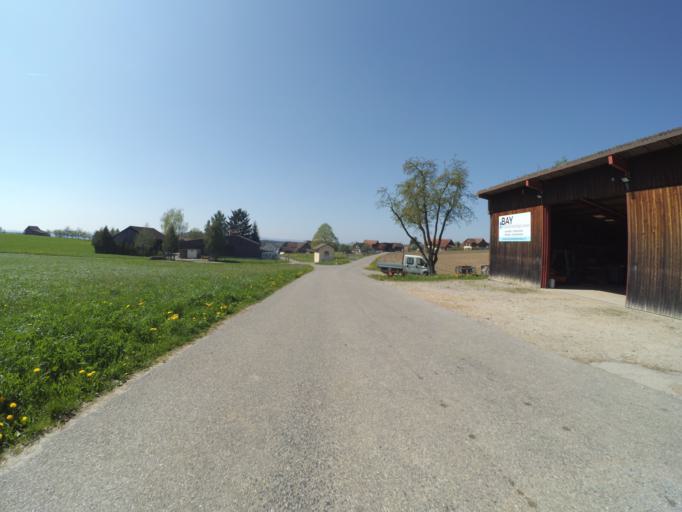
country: CH
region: Zurich
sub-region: Bezirk Andelfingen
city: Kleinandelfingen
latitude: 47.6290
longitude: 8.7325
